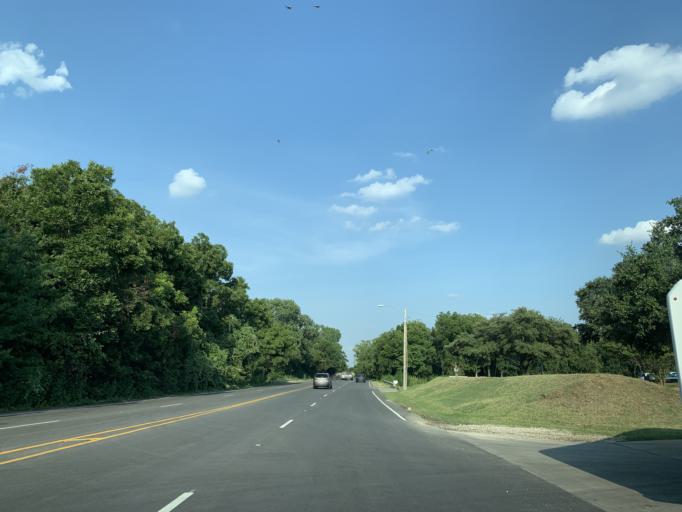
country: US
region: Texas
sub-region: Tarrant County
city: Hurst
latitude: 32.8022
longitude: -97.1808
